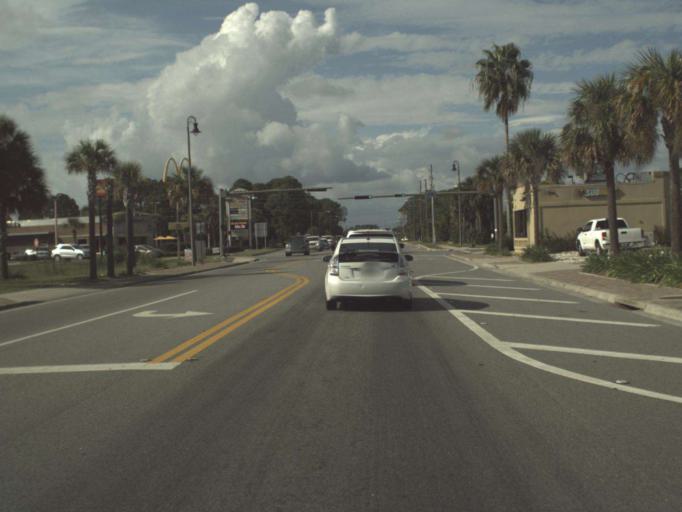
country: US
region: Florida
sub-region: Gulf County
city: Port Saint Joe
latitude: 29.8150
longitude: -85.3046
